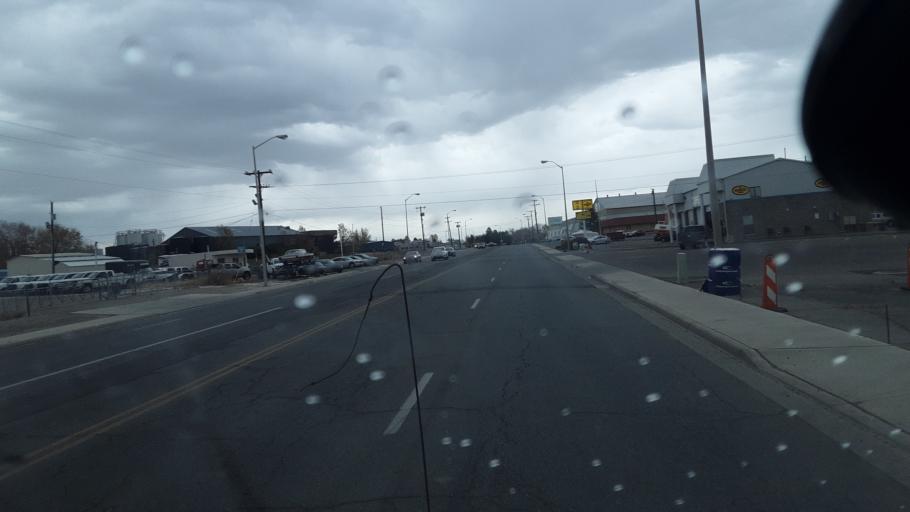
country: US
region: New Mexico
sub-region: San Juan County
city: Farmington
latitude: 36.7380
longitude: -108.1752
